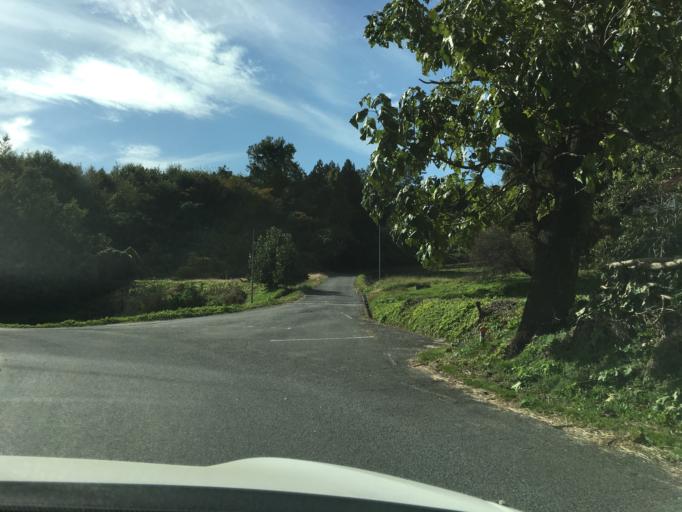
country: JP
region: Fukushima
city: Miharu
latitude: 37.5143
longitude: 140.5004
